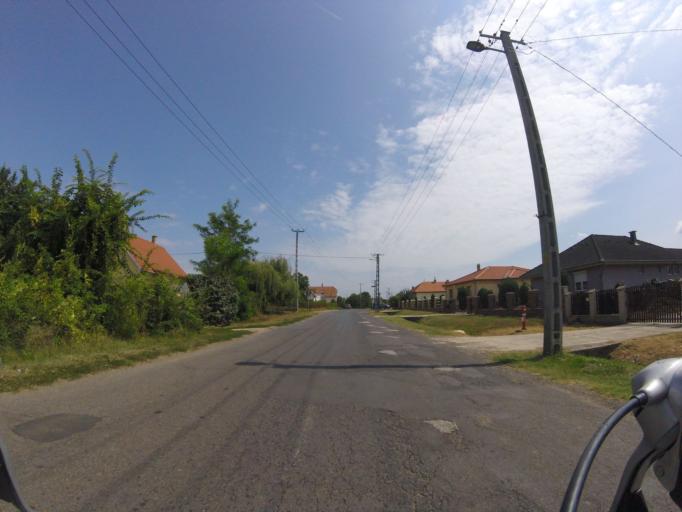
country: HU
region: Szabolcs-Szatmar-Bereg
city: Nyirbogdany
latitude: 48.0608
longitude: 21.8694
